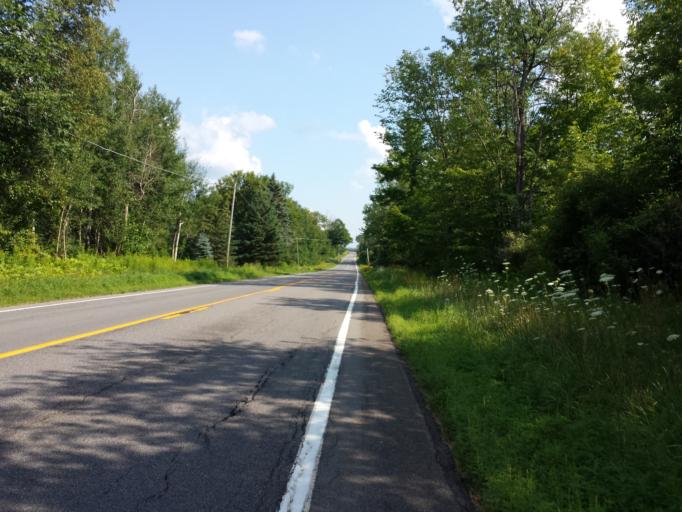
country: US
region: New York
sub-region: St. Lawrence County
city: Hannawa Falls
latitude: 44.6371
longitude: -74.9597
